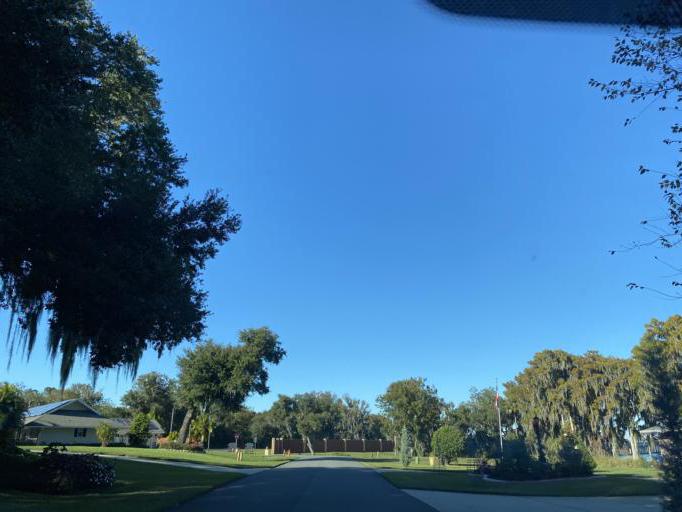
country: US
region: Florida
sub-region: Lake County
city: Howie In The Hills
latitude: 28.7326
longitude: -81.7679
